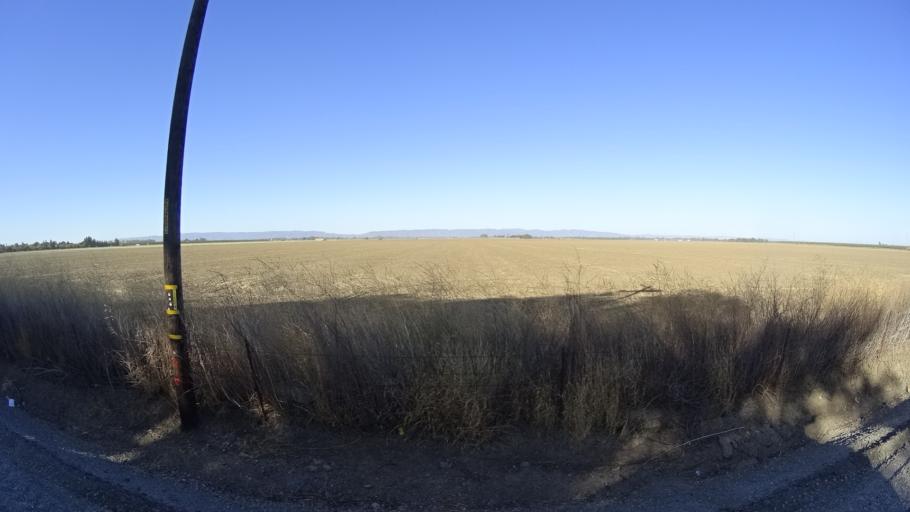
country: US
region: California
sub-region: Yolo County
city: Davis
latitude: 38.5668
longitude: -121.7861
